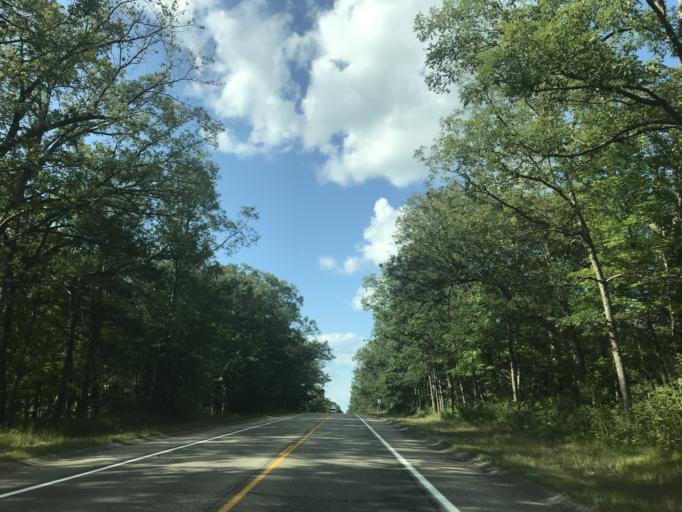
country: US
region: Michigan
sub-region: Newaygo County
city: White Cloud
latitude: 43.5164
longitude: -85.7721
